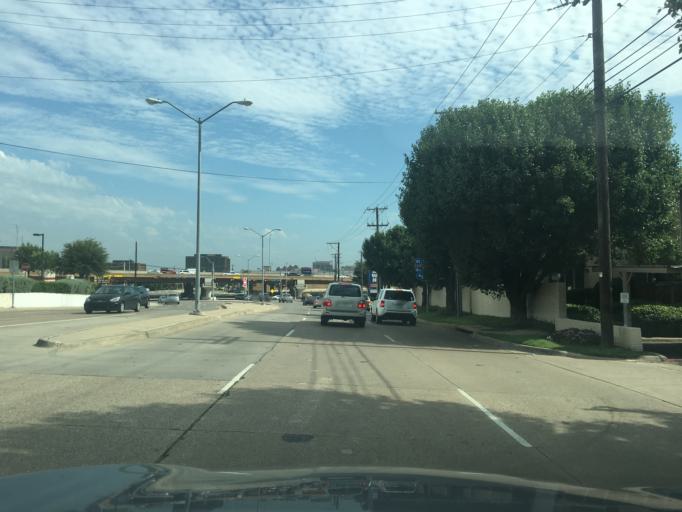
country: US
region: Texas
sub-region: Dallas County
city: Addison
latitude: 32.9231
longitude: -96.8381
